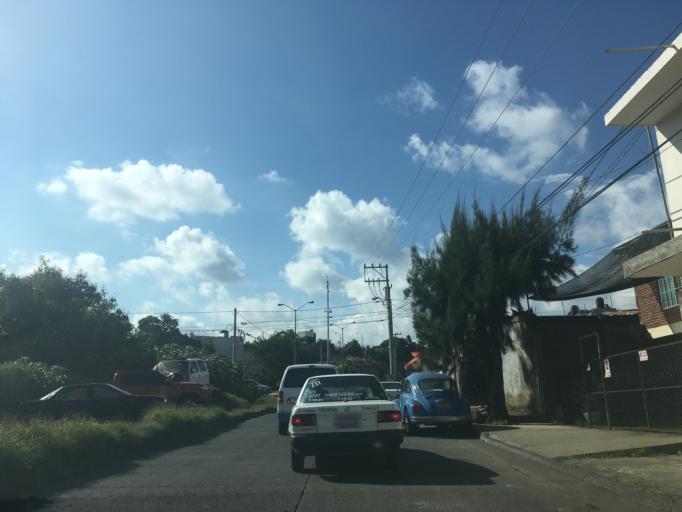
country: MX
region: Michoacan
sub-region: Uruapan
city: Uruapan
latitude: 19.4098
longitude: -102.0697
